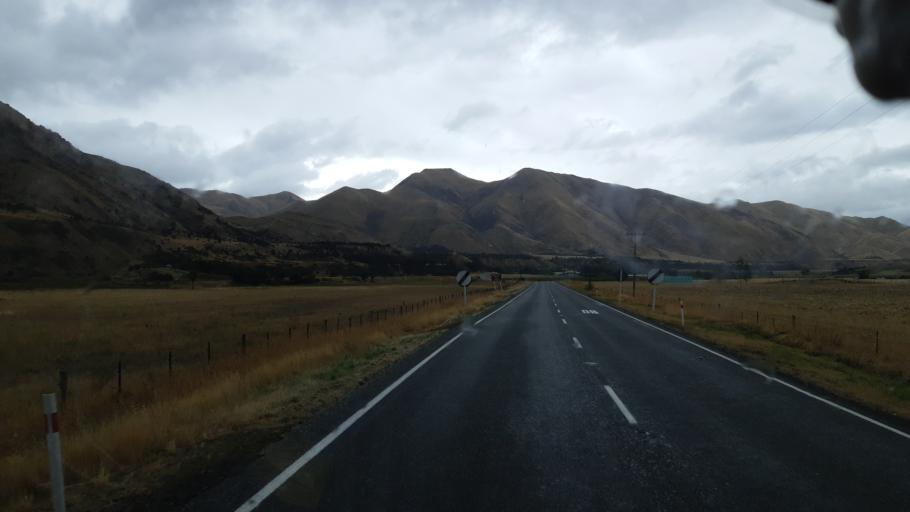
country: NZ
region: Canterbury
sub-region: Hurunui District
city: Amberley
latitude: -42.6276
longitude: 172.7676
